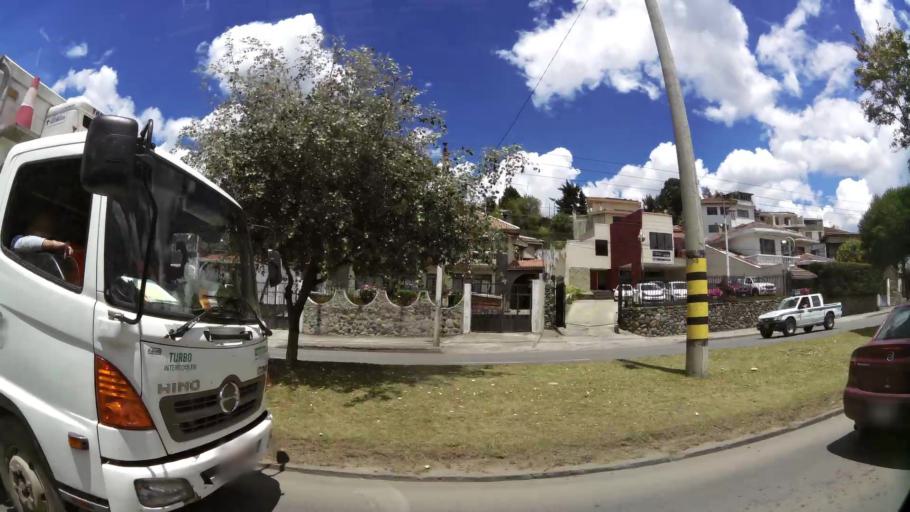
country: EC
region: Azuay
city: Cuenca
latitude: -2.8880
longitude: -79.0104
